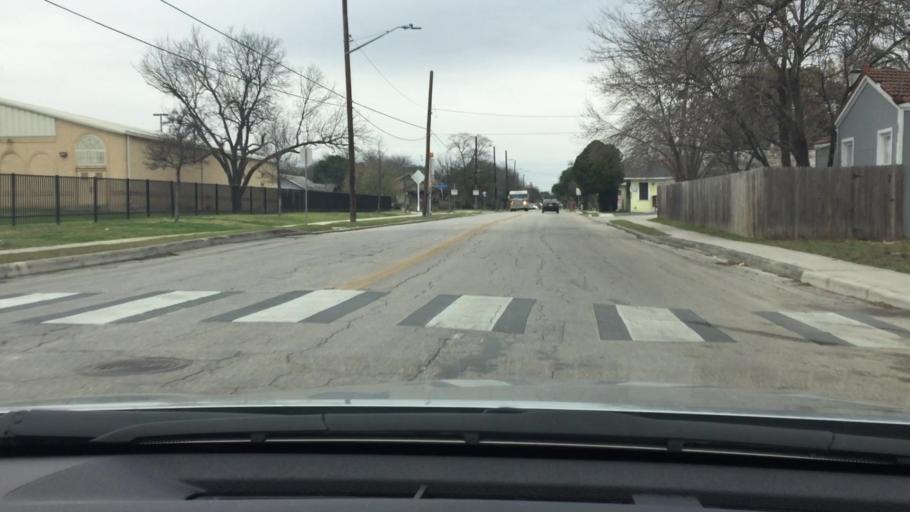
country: US
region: Texas
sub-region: Bexar County
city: Balcones Heights
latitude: 29.4560
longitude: -98.5236
